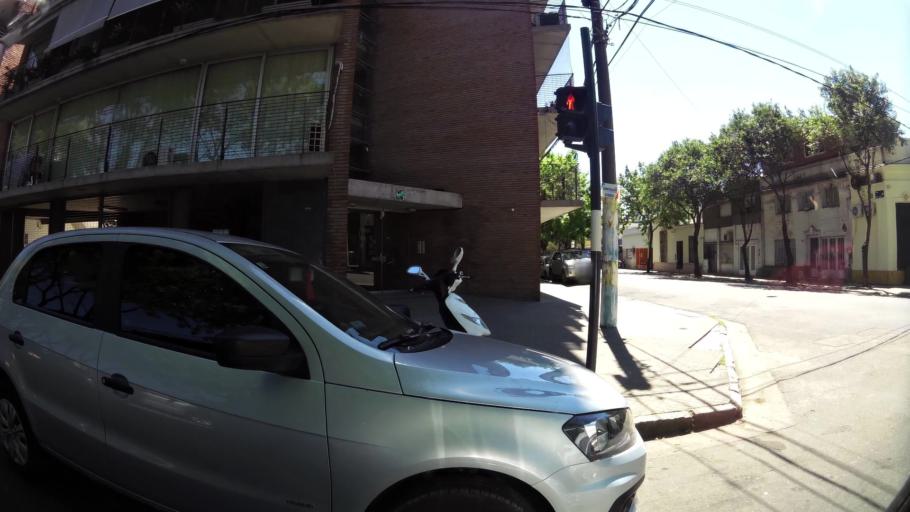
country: AR
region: Santa Fe
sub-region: Departamento de Rosario
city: Rosario
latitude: -32.9327
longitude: -60.6605
